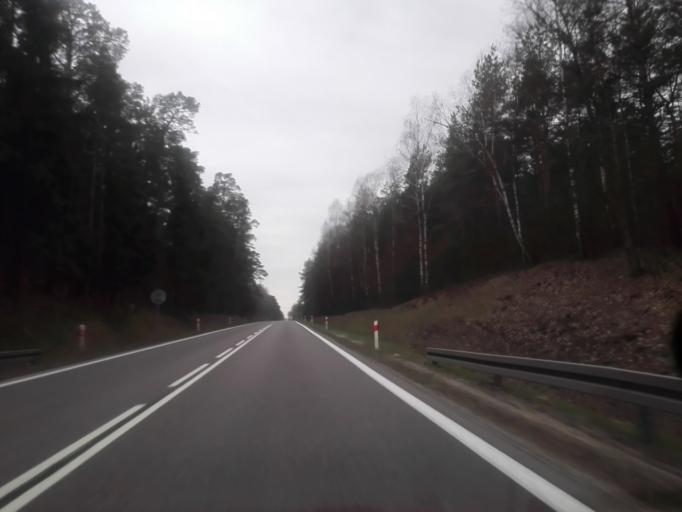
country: PL
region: Podlasie
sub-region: Powiat grajewski
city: Rajgrod
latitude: 53.6973
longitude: 22.6487
